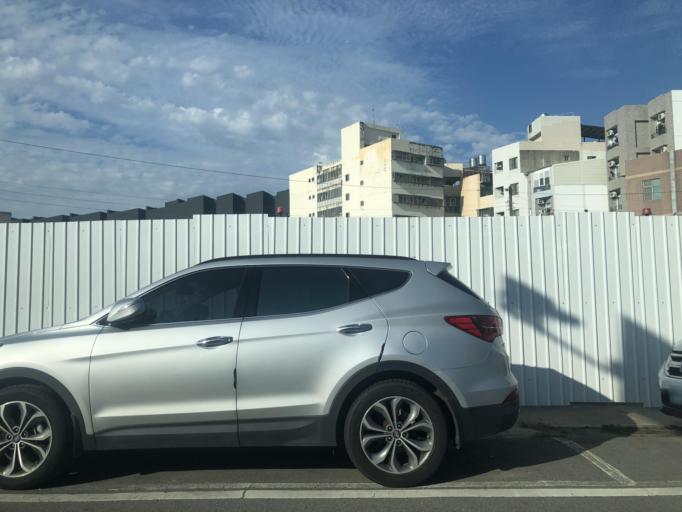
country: TW
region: Taiwan
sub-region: Tainan
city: Tainan
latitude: 23.0222
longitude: 120.2206
